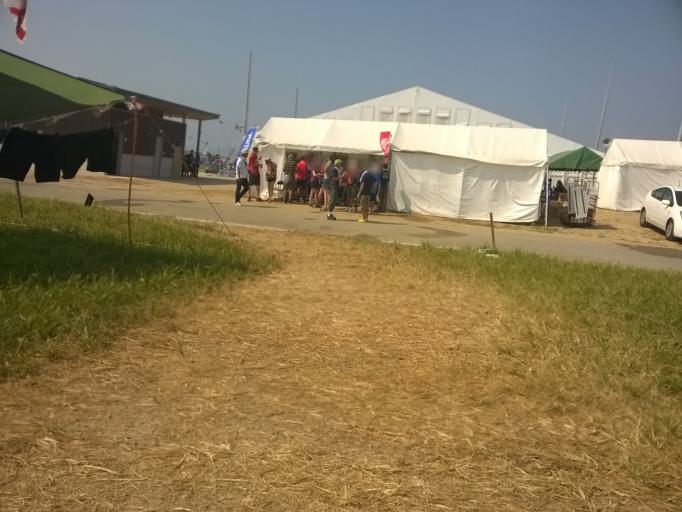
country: JP
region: Yamaguchi
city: Ogori-shimogo
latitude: 34.0131
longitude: 131.3779
